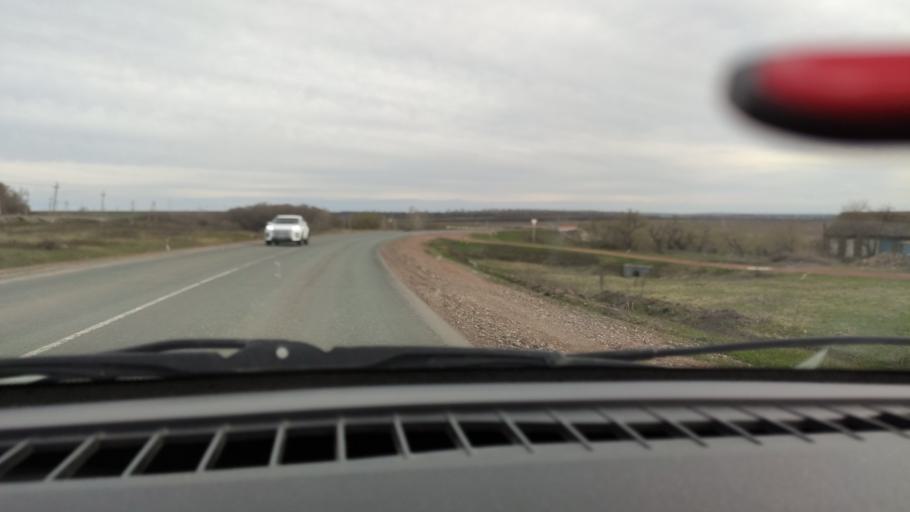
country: RU
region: Bashkortostan
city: Yermolayevo
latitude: 52.4760
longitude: 55.8302
